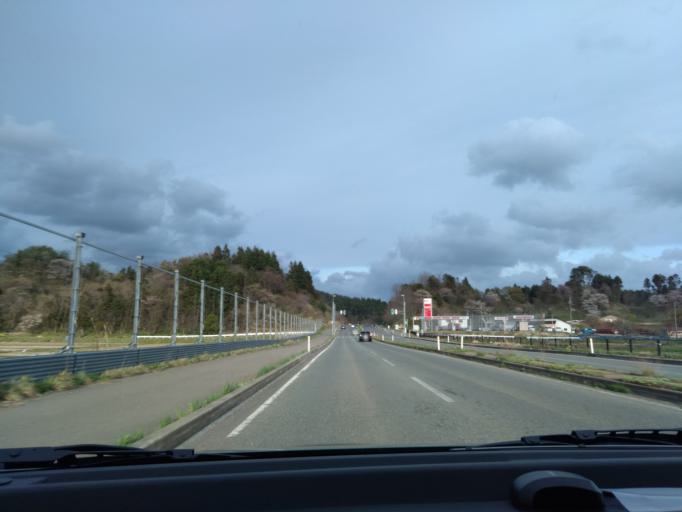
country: JP
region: Akita
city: Akita
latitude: 39.7523
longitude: 140.1161
